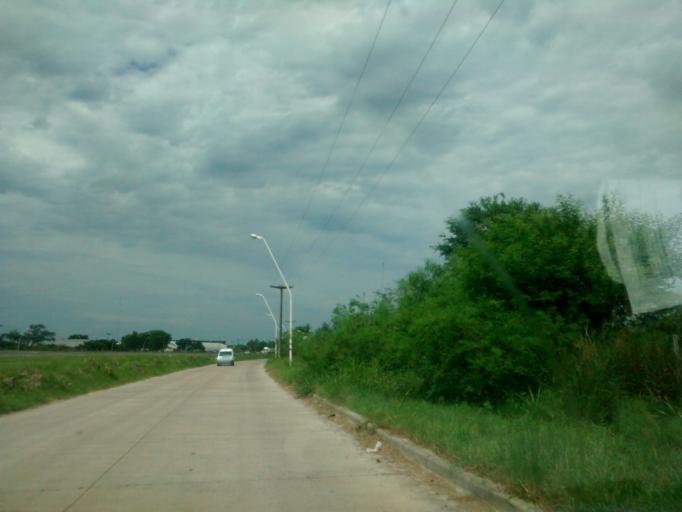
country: AR
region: Chaco
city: Fontana
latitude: -27.4095
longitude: -58.9879
